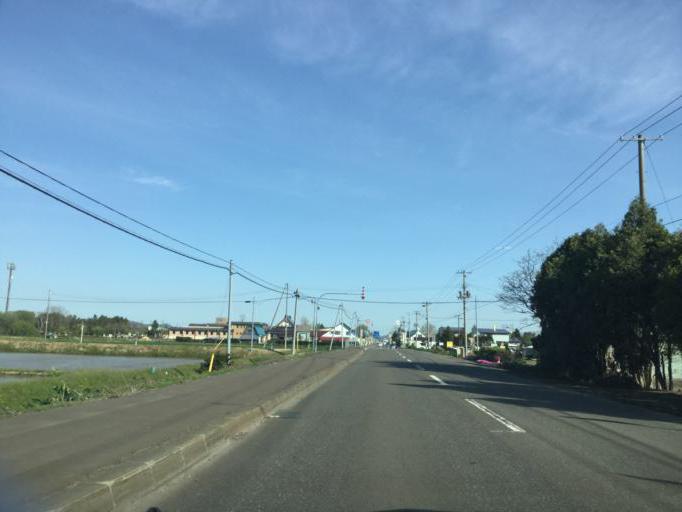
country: JP
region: Hokkaido
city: Ebetsu
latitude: 43.0733
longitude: 141.6461
